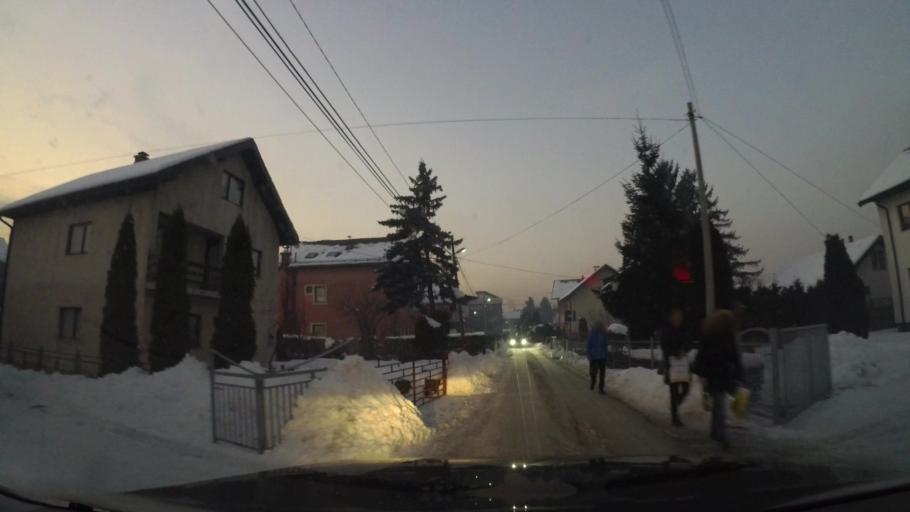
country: BA
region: Federation of Bosnia and Herzegovina
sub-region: Kanton Sarajevo
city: Sarajevo
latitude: 43.8360
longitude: 18.3201
